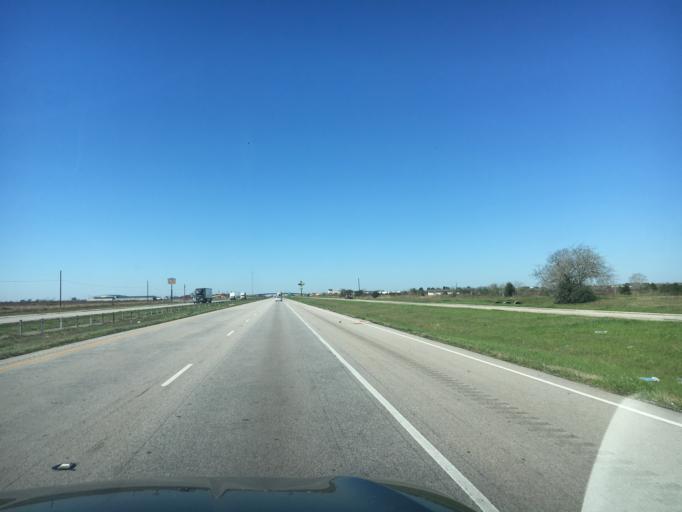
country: US
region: Texas
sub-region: Colorado County
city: Eagle Lake
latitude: 29.7442
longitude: -96.3178
